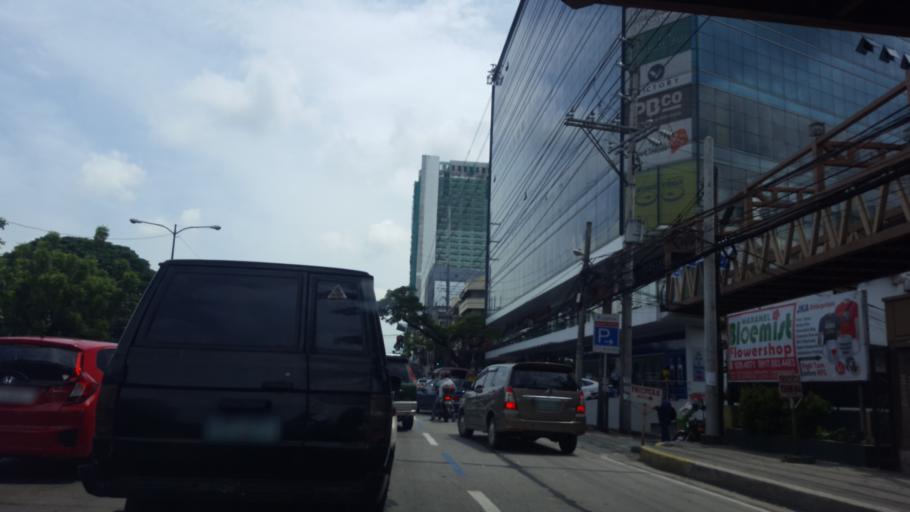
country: PH
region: Metro Manila
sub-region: Marikina
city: Calumpang
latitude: 14.6413
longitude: 121.0745
